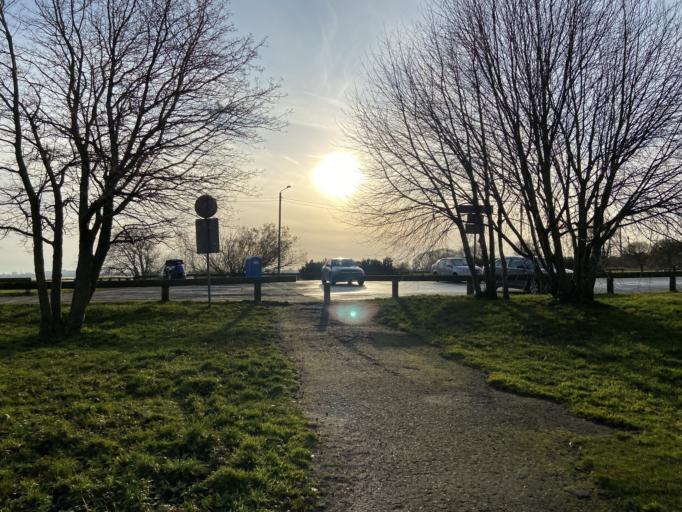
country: EE
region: Harju
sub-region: Tallinna linn
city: Tallinn
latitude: 59.4733
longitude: 24.7228
